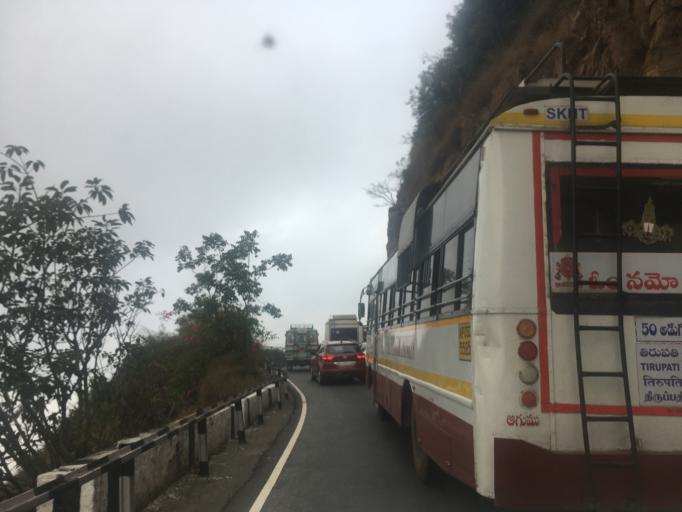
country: IN
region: Andhra Pradesh
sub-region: Chittoor
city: Tirumala
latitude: 13.6674
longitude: 79.3508
